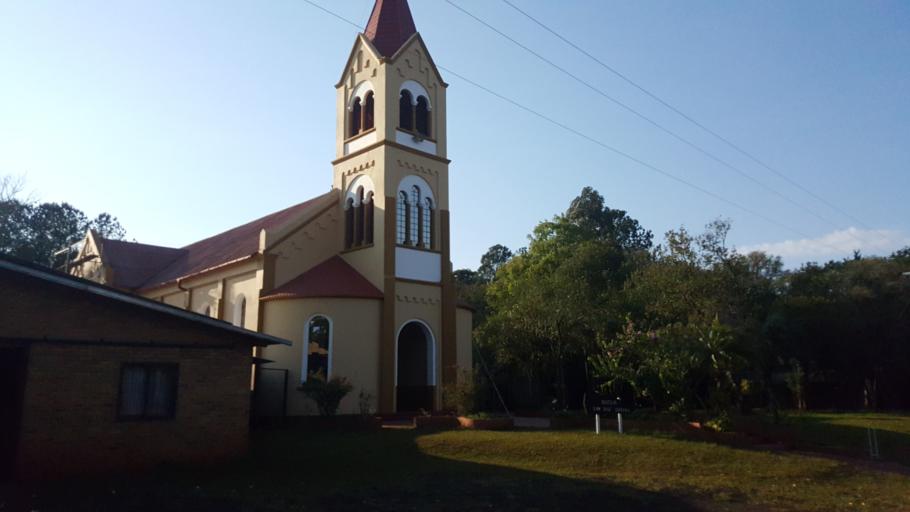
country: AR
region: Misiones
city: Capiovi
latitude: -26.8916
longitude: -55.0589
